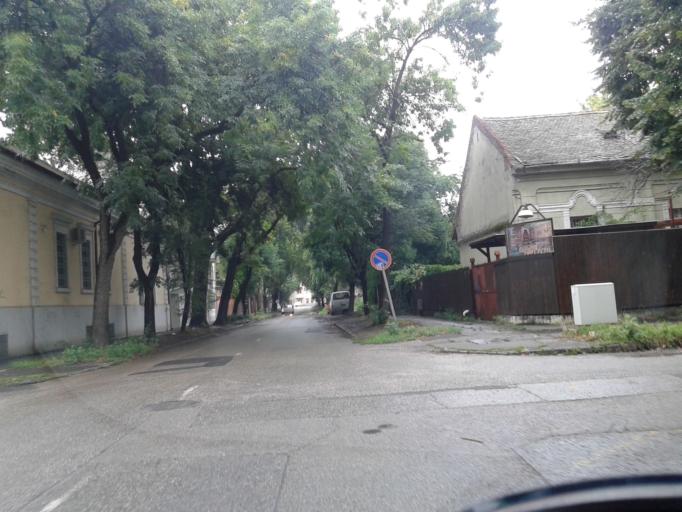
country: HU
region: Csongrad
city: Szeged
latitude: 46.2578
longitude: 20.1618
